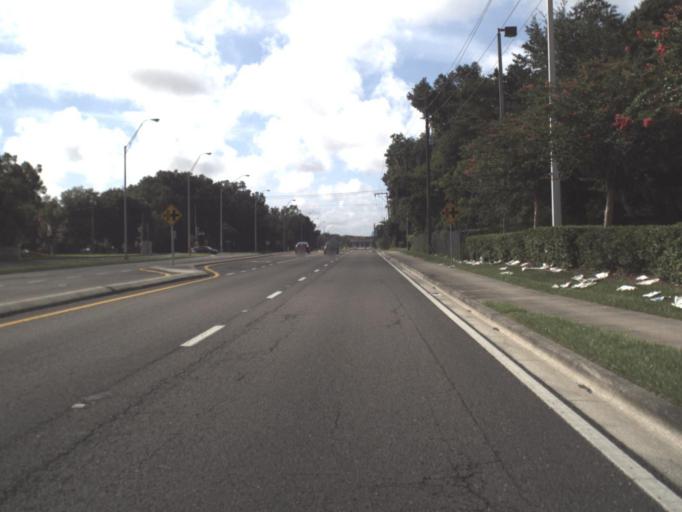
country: US
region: Florida
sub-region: Hillsborough County
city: Lake Magdalene
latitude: 28.1069
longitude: -82.4583
